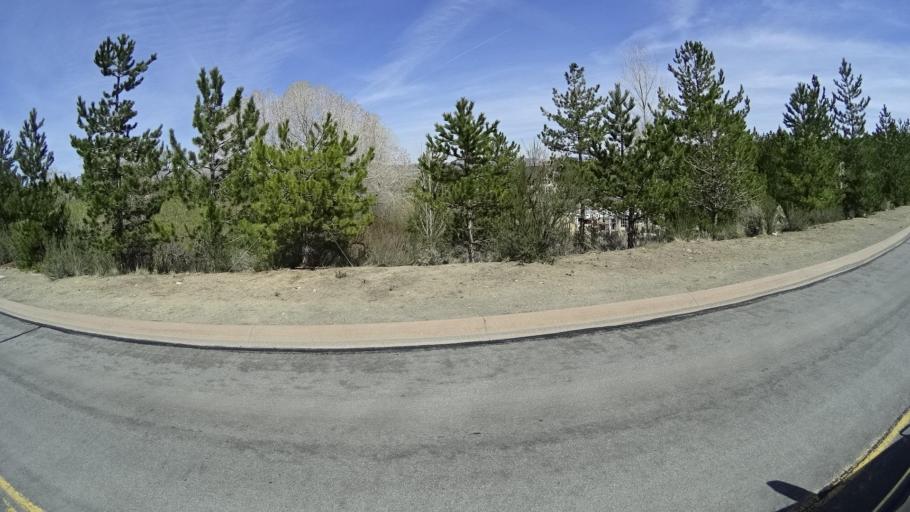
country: US
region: Nevada
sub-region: Washoe County
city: Mogul
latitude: 39.4856
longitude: -119.8710
